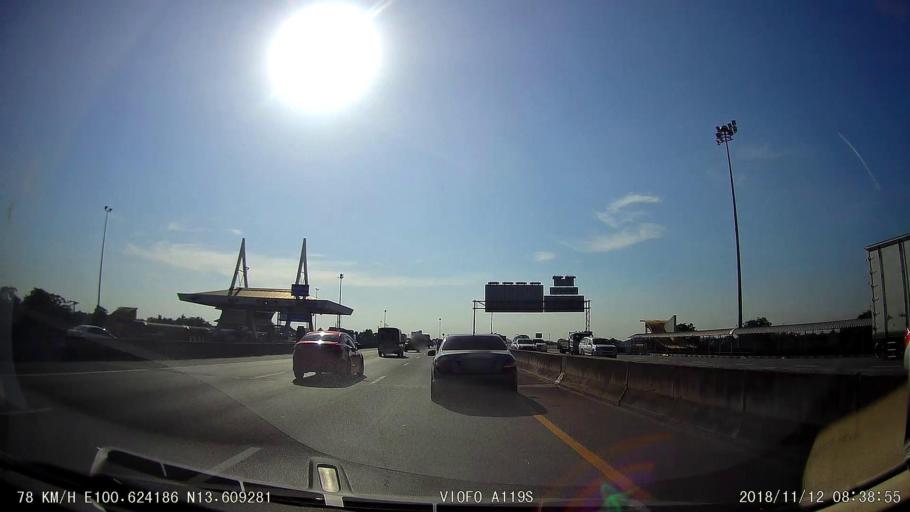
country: TH
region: Samut Prakan
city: Samut Prakan
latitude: 13.6091
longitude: 100.6244
